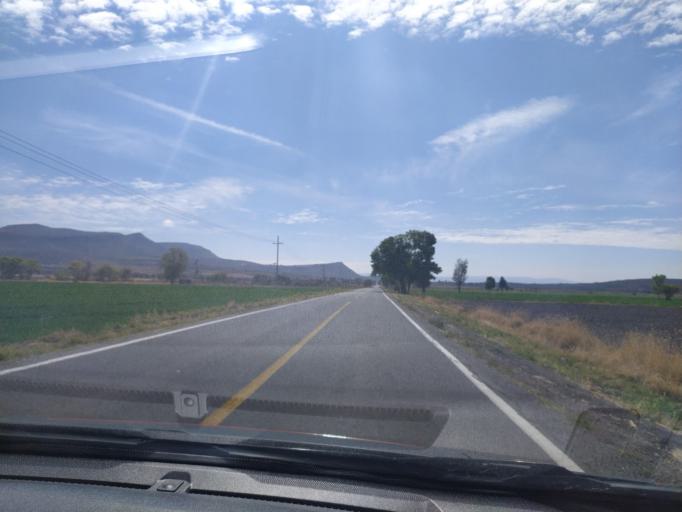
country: MX
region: Guanajuato
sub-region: San Francisco del Rincon
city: San Ignacio de Hidalgo
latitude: 20.8449
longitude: -101.8484
